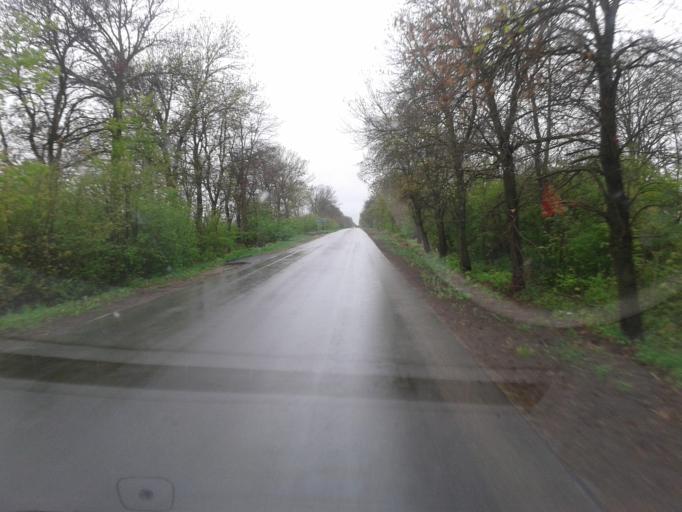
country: PL
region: Lublin Voivodeship
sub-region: Powiat tomaszowski
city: Jarczow
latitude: 50.3670
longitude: 23.6438
